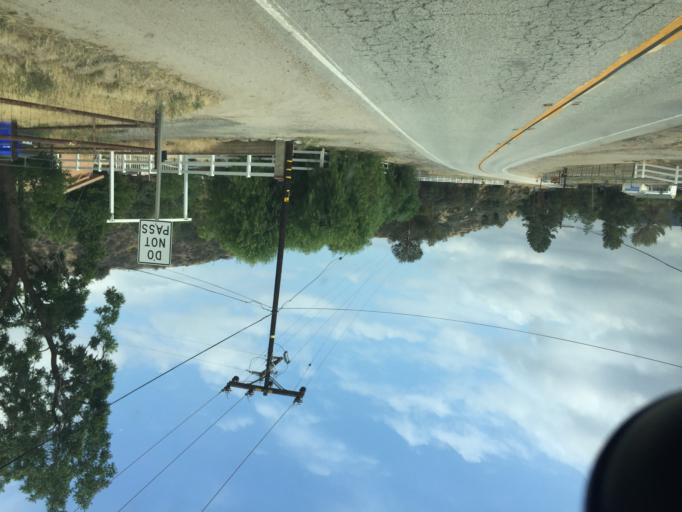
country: US
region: California
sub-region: Los Angeles County
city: Santa Clarita
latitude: 34.4871
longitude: -118.4638
